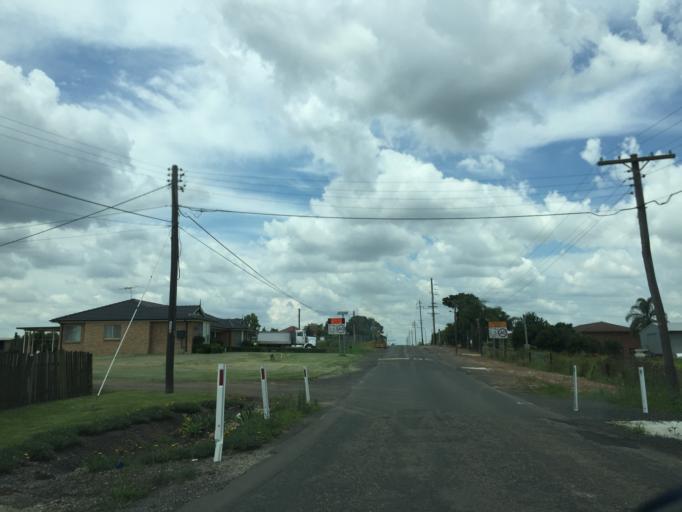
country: AU
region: New South Wales
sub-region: Blacktown
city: Riverstone
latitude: -33.7025
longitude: 150.8873
